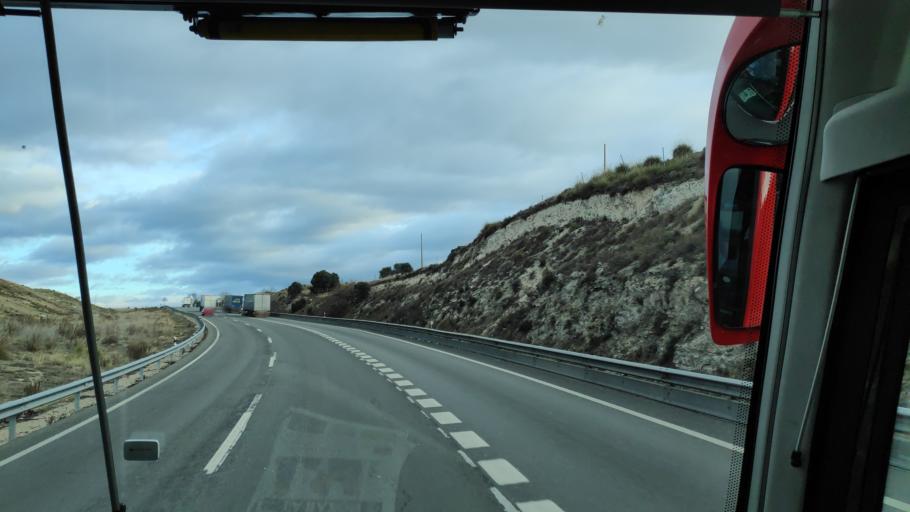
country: ES
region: Madrid
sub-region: Provincia de Madrid
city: Tielmes
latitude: 40.1992
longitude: -3.3136
